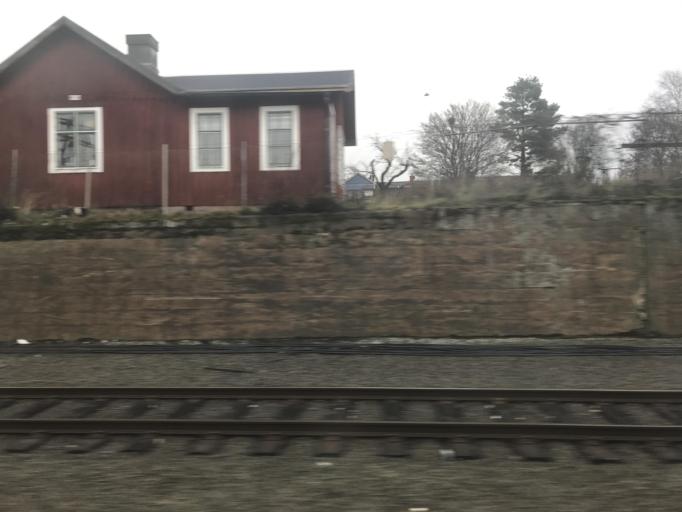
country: SE
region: Joenkoeping
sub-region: Nassjo Kommun
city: Nassjo
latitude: 57.6502
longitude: 14.6970
